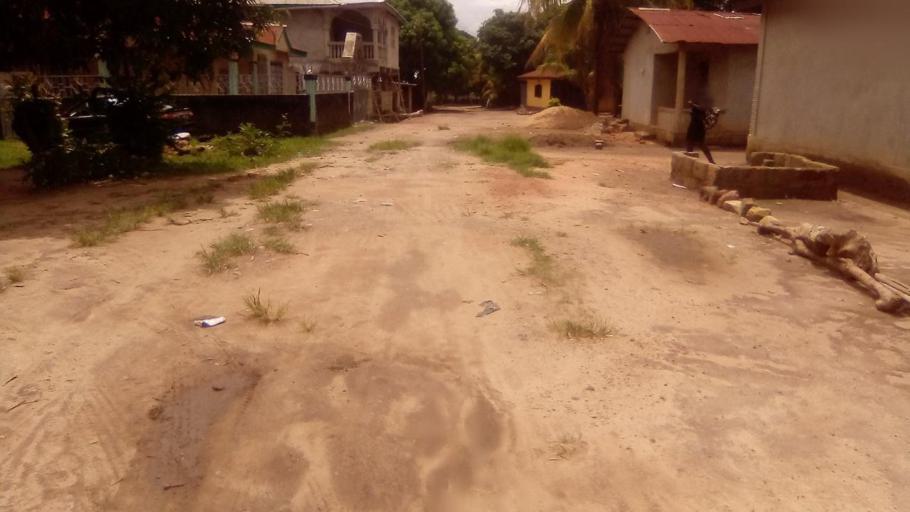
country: SL
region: Southern Province
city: Bo
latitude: 7.9382
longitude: -11.7410
